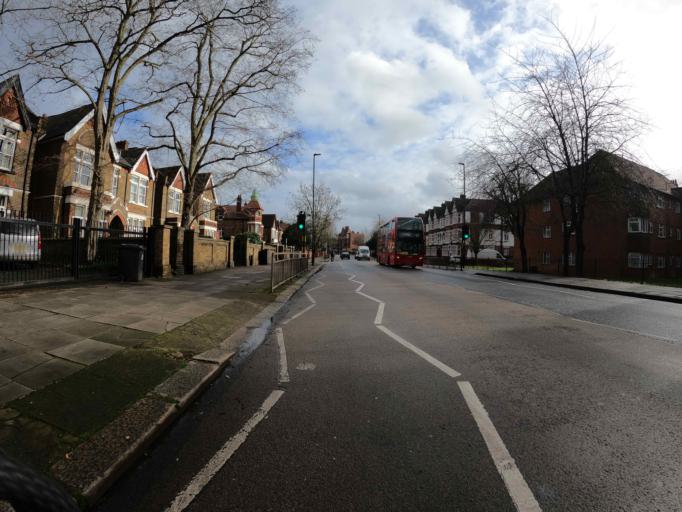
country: GB
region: England
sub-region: Greater London
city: Acton
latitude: 51.5095
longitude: -0.2852
